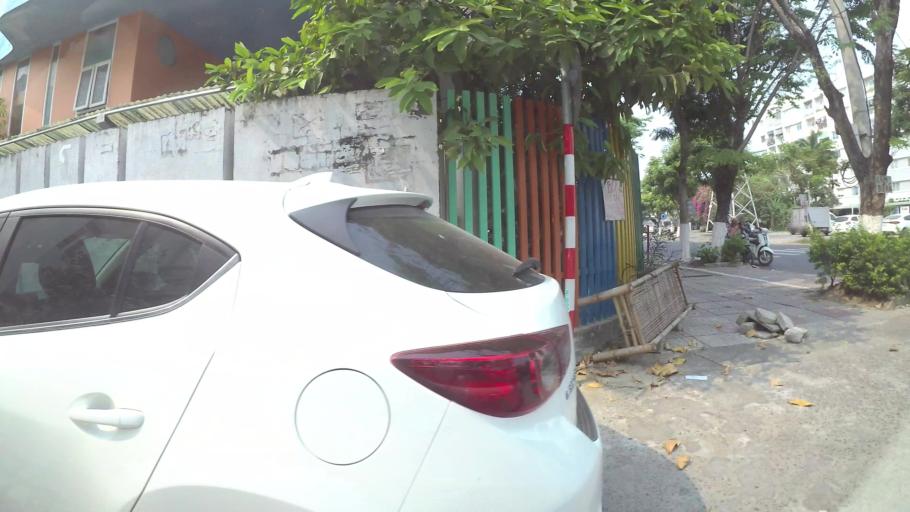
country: VN
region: Da Nang
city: Son Tra
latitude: 16.0441
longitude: 108.2172
